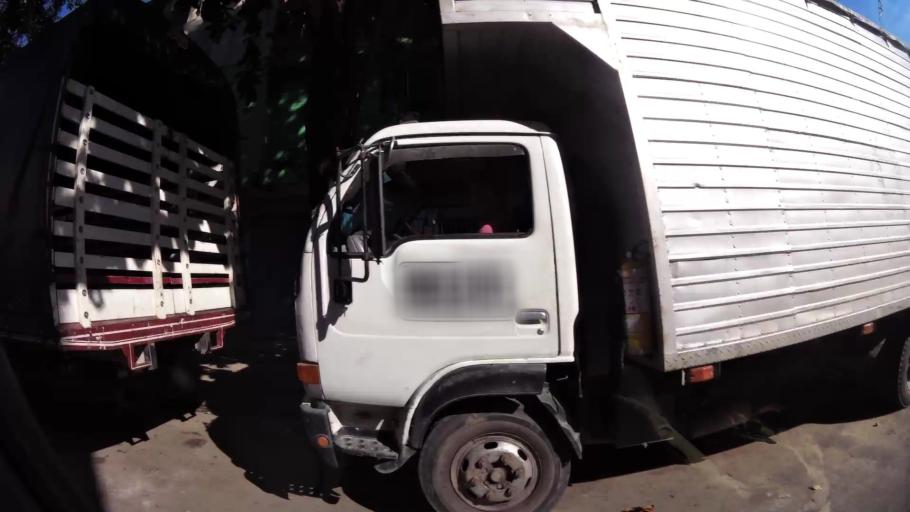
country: CO
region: Atlantico
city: Barranquilla
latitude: 10.9745
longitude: -74.7809
